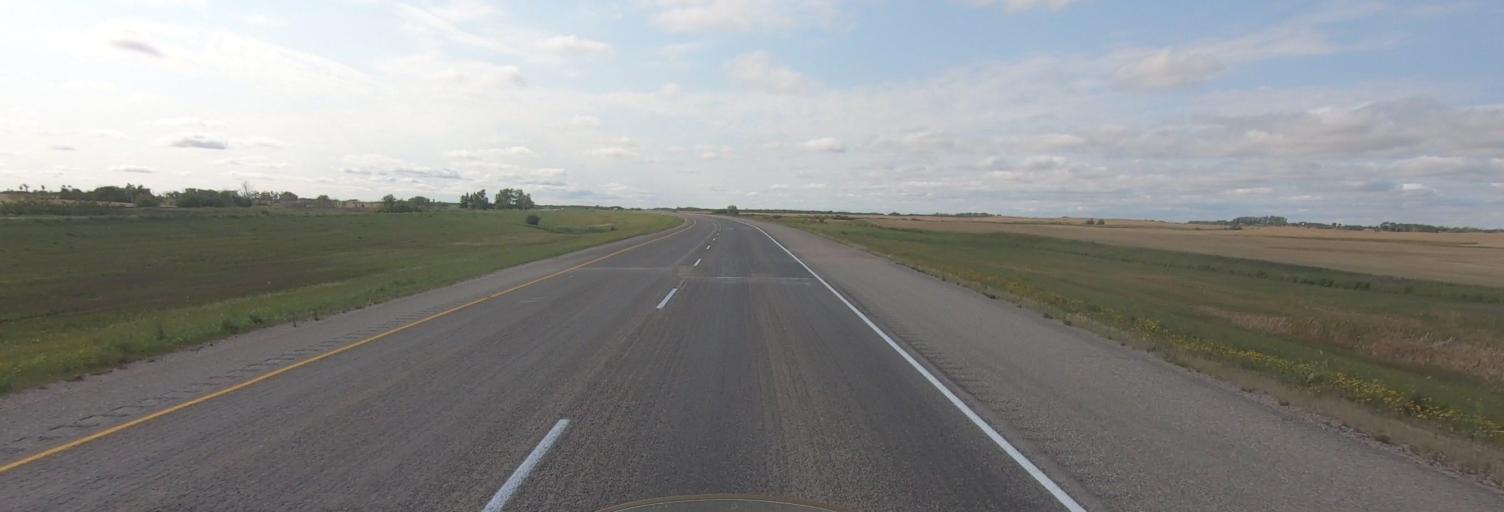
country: CA
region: Saskatchewan
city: Moosomin
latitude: 50.0508
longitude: -101.4259
